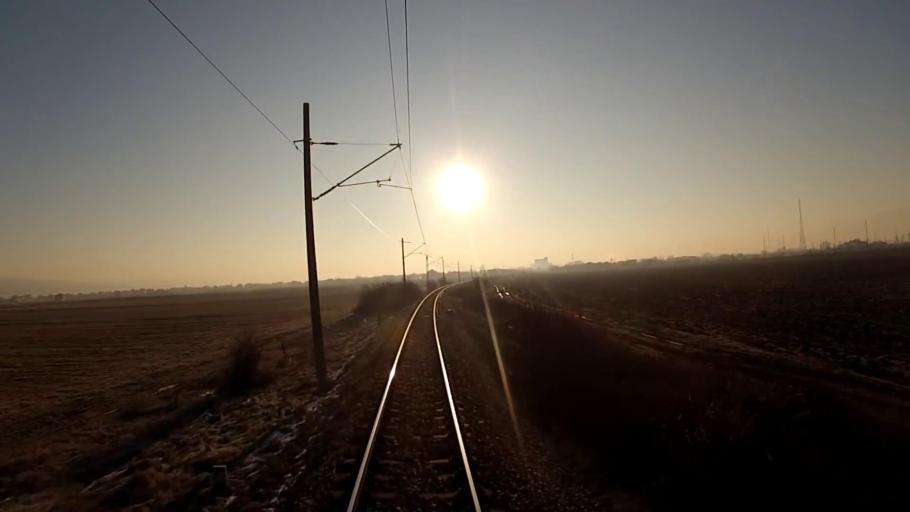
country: BG
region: Sofiya
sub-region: Obshtina Kostinbrod
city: Kostinbrod
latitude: 42.8084
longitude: 23.1976
